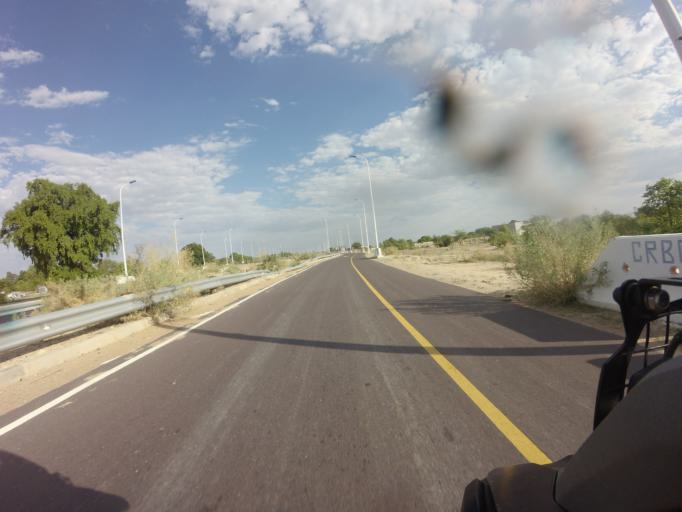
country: AO
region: Cunene
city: Ondjiva
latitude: -17.0077
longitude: 15.6456
